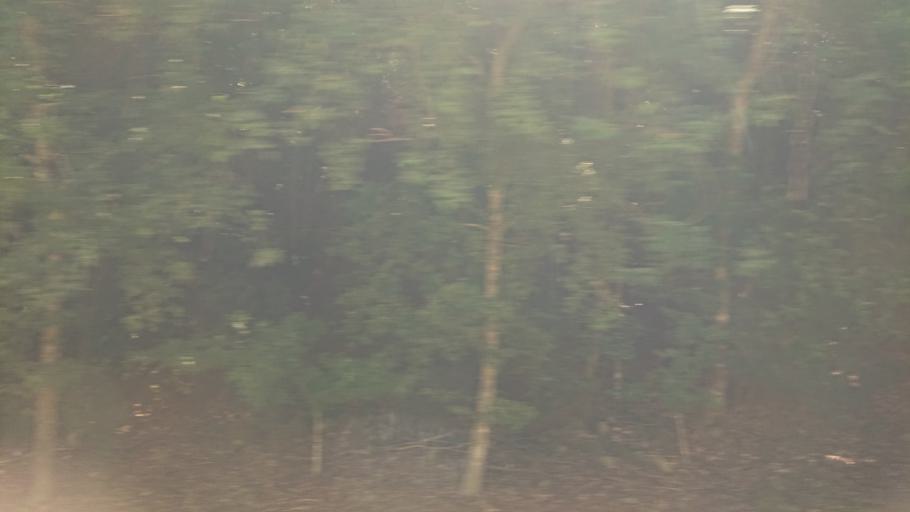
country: TW
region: Taiwan
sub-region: Nantou
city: Puli
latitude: 24.0517
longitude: 120.9345
